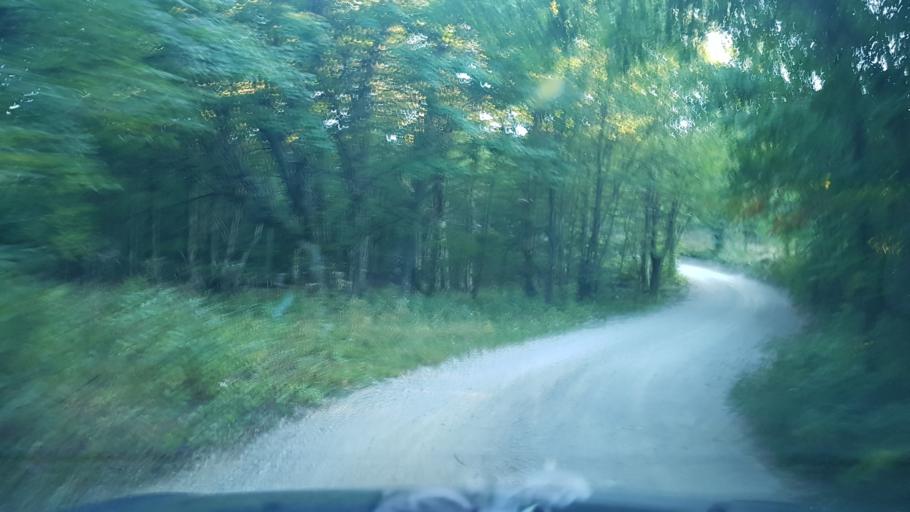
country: SI
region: Vipava
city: Vipava
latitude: 45.7789
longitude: 14.0453
